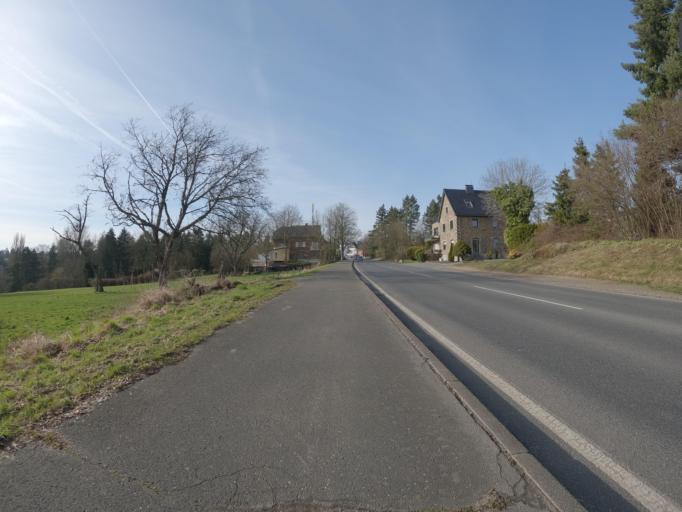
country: DE
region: North Rhine-Westphalia
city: Stolberg
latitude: 50.7526
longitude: 6.1880
